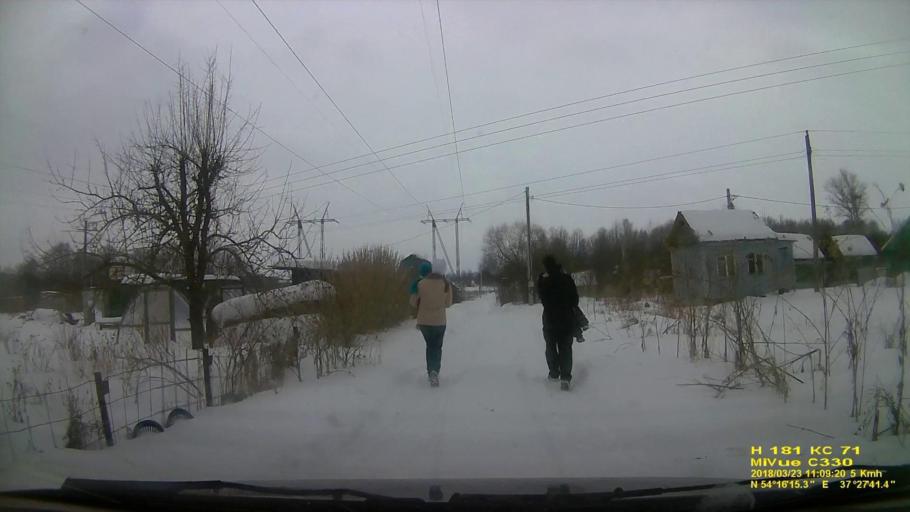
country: RU
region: Tula
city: Leninskiy
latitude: 54.2709
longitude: 37.4614
